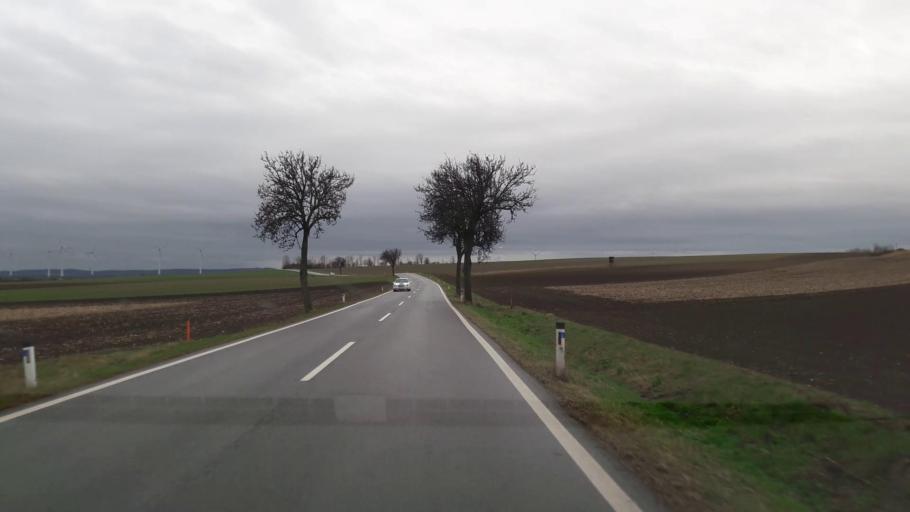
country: AT
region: Lower Austria
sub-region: Politischer Bezirk Bruck an der Leitha
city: Scharndorf
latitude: 48.0865
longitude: 16.7969
